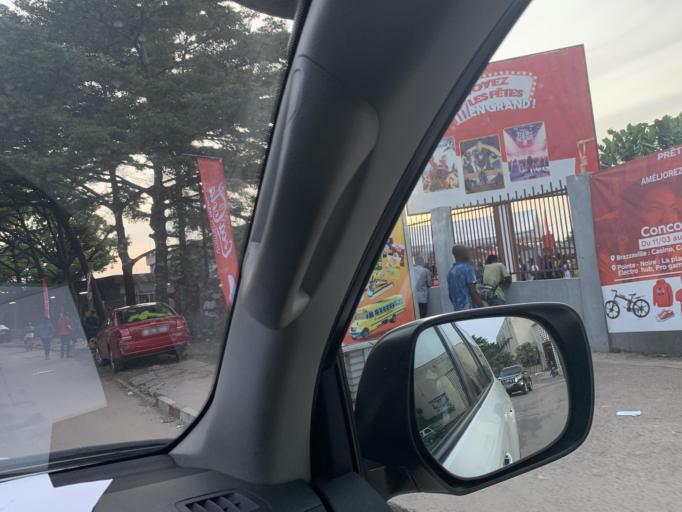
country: CG
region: Brazzaville
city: Brazzaville
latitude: -4.2671
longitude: 15.2845
